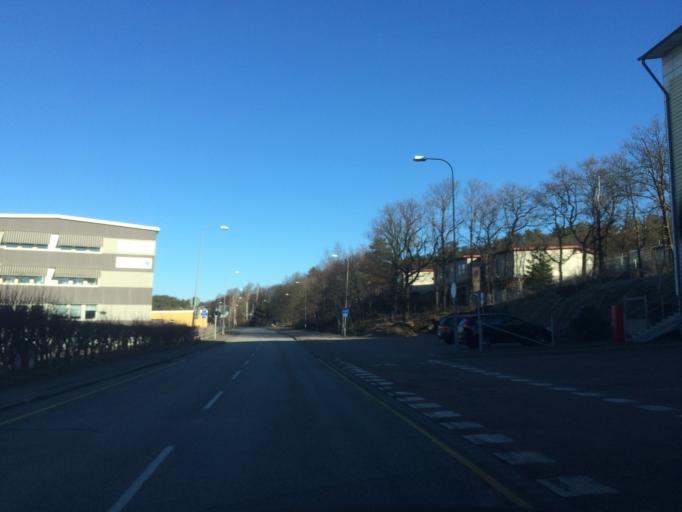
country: SE
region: Vaestra Goetaland
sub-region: Goteborg
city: Majorna
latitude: 57.6599
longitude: 11.8988
